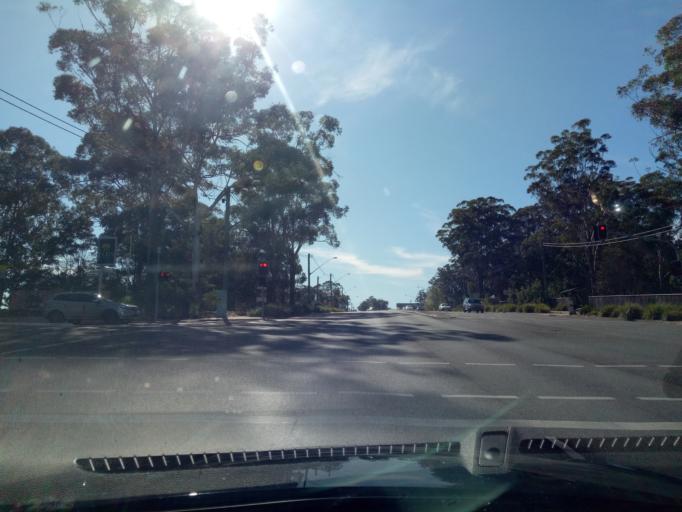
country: AU
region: New South Wales
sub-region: Gosford Shire
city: Erina
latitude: -33.4260
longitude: 151.3987
